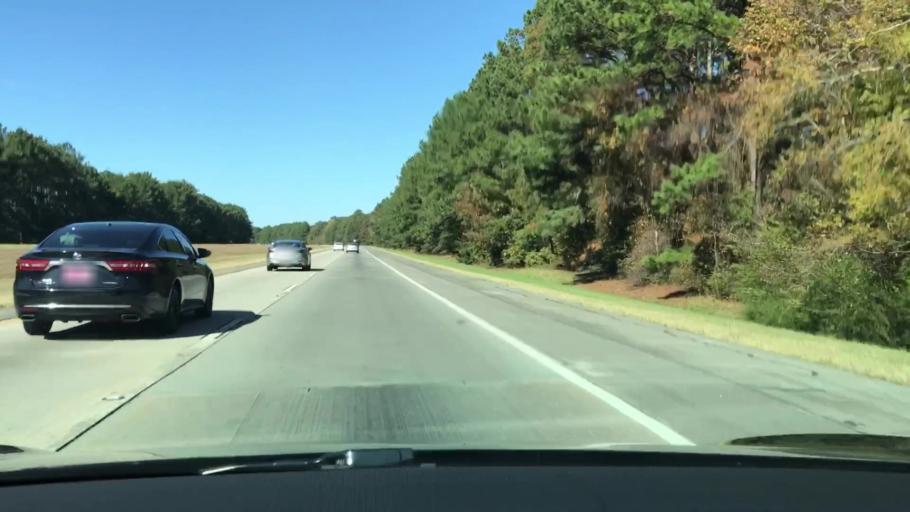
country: US
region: Georgia
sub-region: Taliaferro County
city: Crawfordville
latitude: 33.5349
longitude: -82.9925
